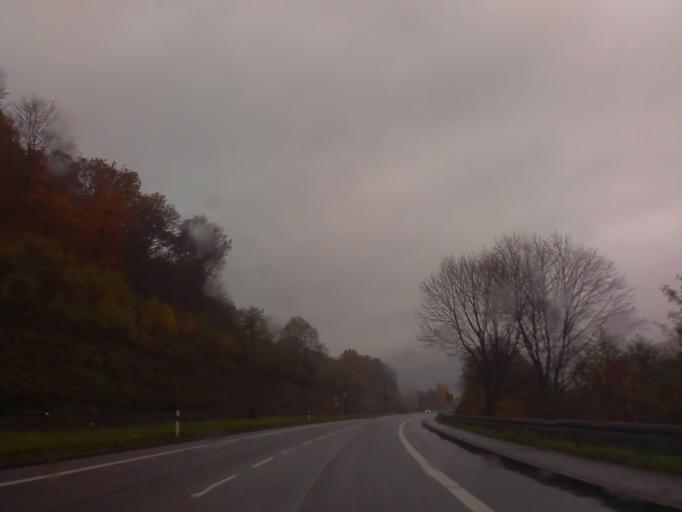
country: DE
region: Hesse
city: Hirschhorn
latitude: 49.4311
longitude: 8.8929
